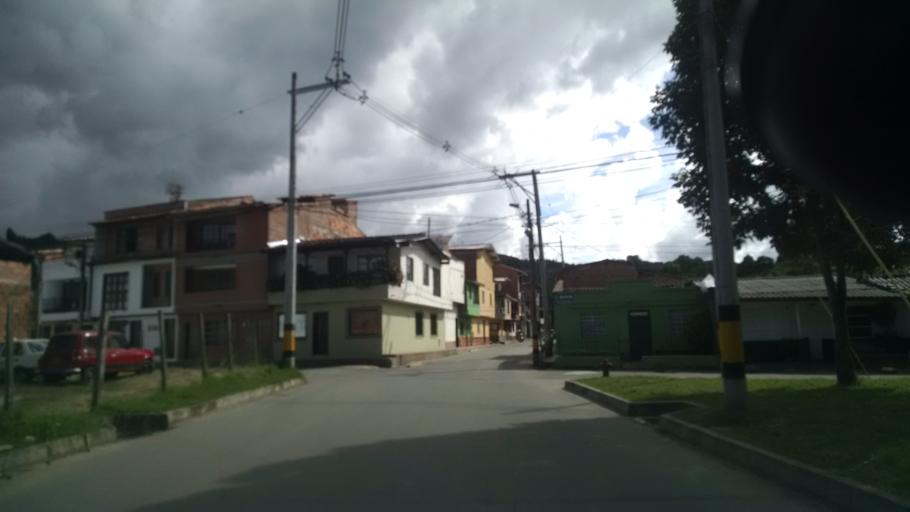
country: CO
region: Antioquia
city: El Retiro
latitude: 6.0610
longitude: -75.5042
